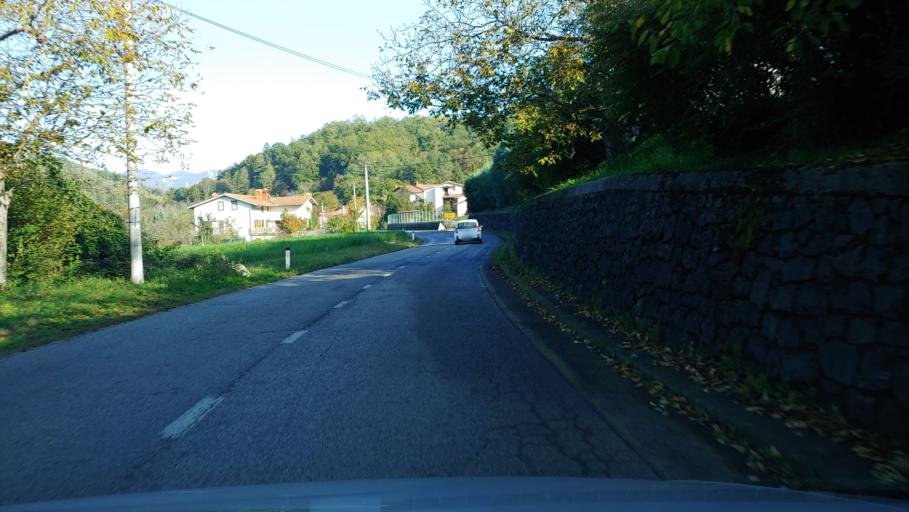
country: SI
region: Ajdovscina
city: Ajdovscina
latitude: 45.8120
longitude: 13.8809
